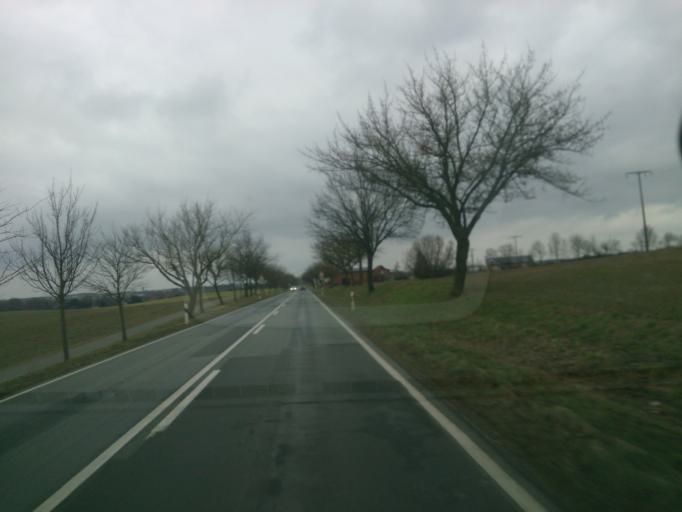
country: DE
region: Mecklenburg-Vorpommern
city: Wackerow
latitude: 53.6772
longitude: 12.9069
